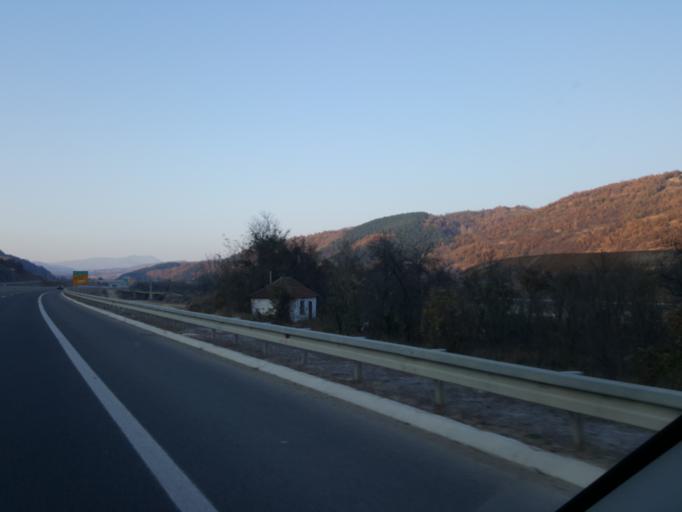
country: RS
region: Central Serbia
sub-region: Pirotski Okrug
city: Pirot
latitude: 43.1803
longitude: 22.5676
